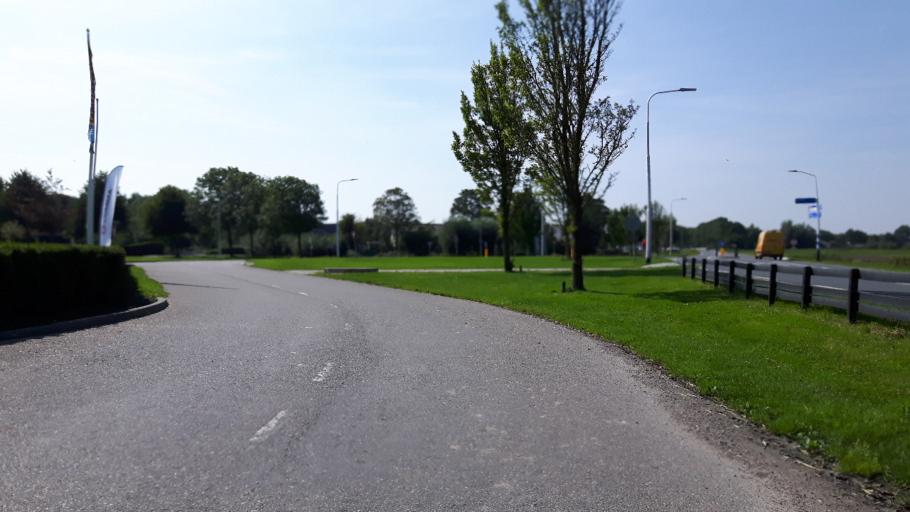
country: NL
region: Friesland
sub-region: Gemeente Ferwerderadiel
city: Hallum
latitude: 53.3106
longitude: 5.7854
